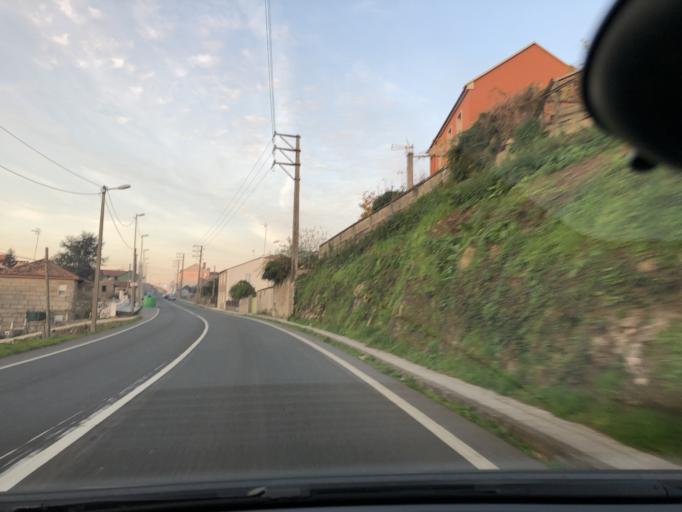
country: ES
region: Galicia
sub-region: Provincia de Pontevedra
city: Marin
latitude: 42.3837
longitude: -8.7141
